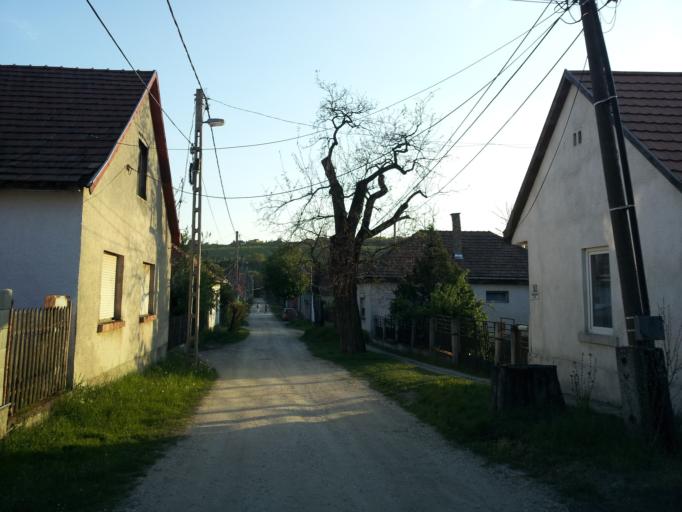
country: HU
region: Pest
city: Piliscsaba
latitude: 47.6276
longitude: 18.8305
